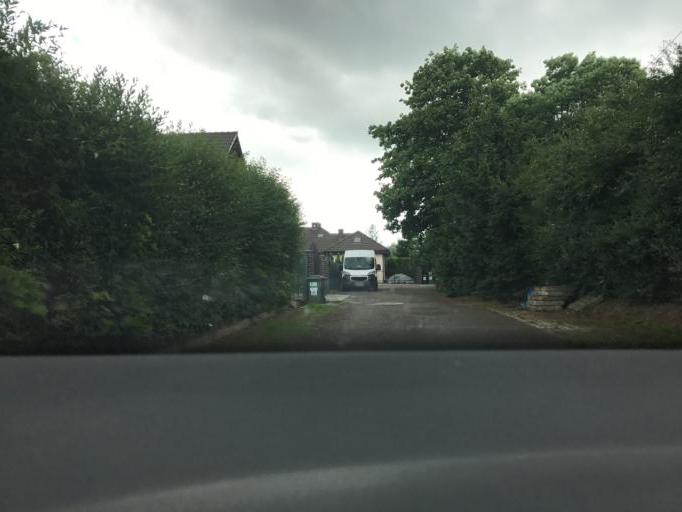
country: PL
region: Pomeranian Voivodeship
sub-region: Powiat gdanski
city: Cedry Wielkie
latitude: 54.3392
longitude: 18.8173
